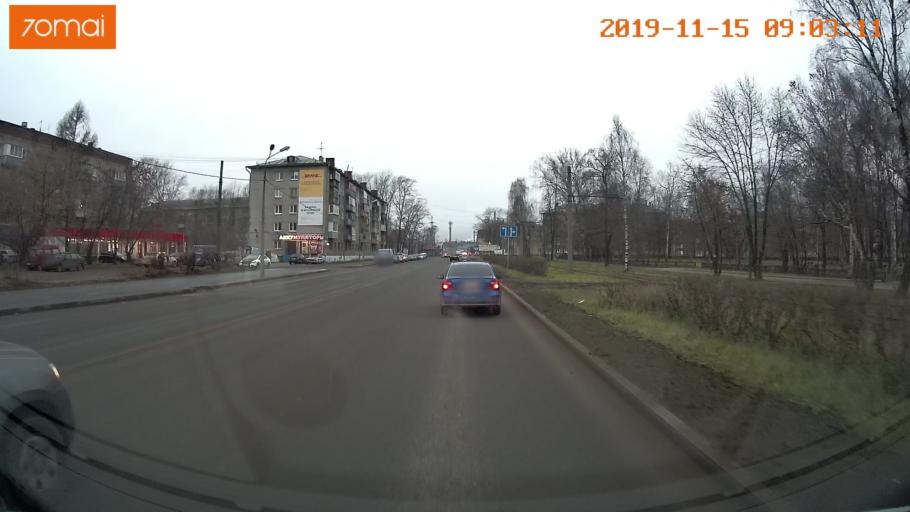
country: RU
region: Vologda
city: Cherepovets
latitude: 59.1377
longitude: 37.9238
